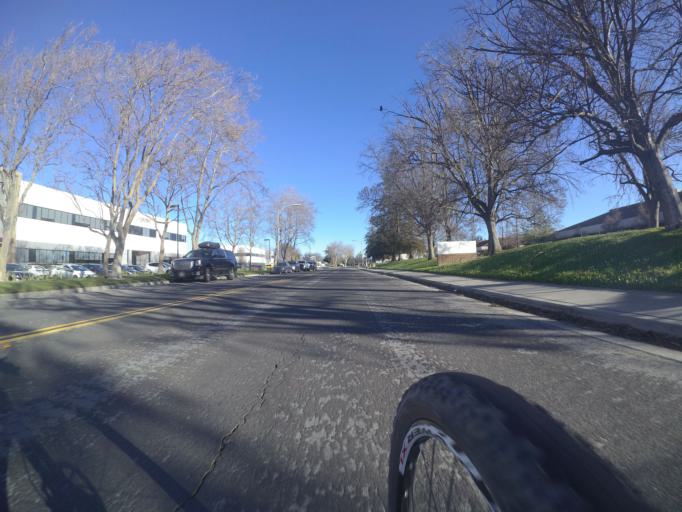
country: US
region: California
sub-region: Santa Clara County
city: Milpitas
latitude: 37.4165
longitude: -121.9510
